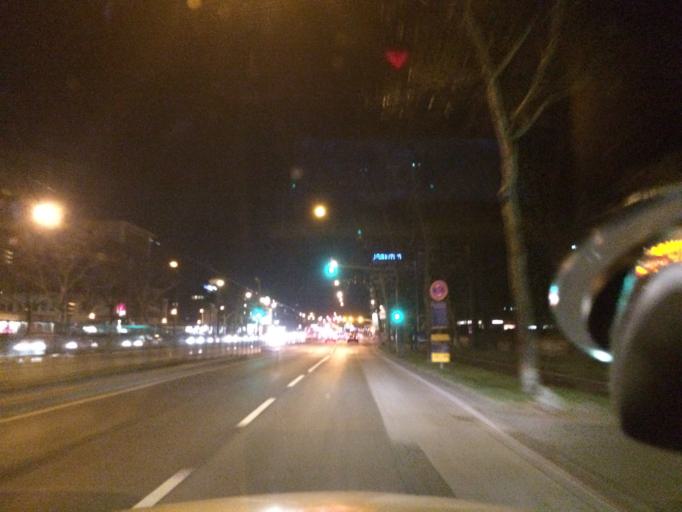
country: DE
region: Hesse
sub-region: Regierungsbezirk Darmstadt
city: Darmstadt
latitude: 49.8709
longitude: 8.6359
